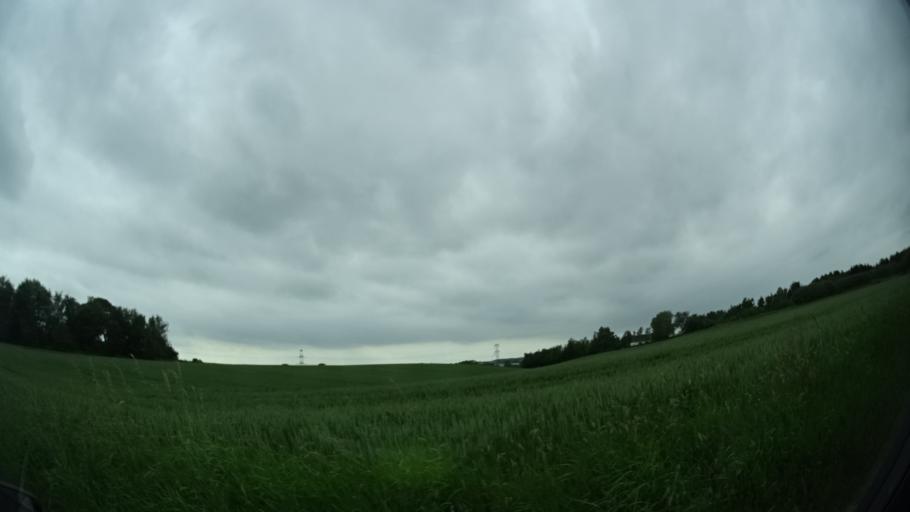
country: DK
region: Central Jutland
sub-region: Arhus Kommune
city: Kolt
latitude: 56.0926
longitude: 10.0744
